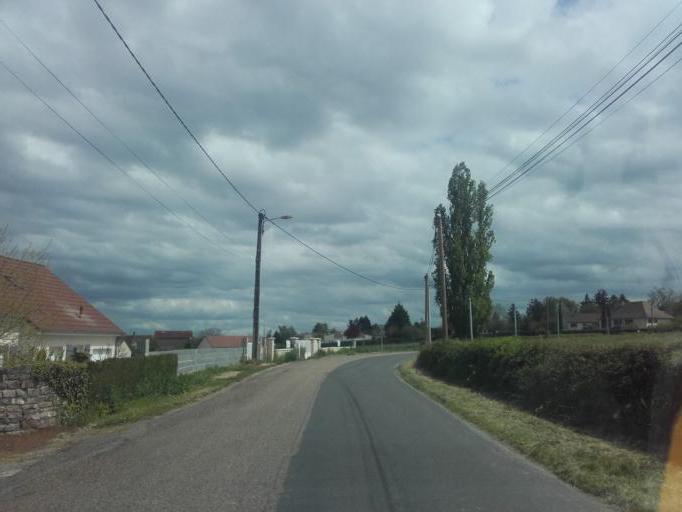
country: FR
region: Bourgogne
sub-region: Departement de Saone-et-Loire
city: Saint-Remy
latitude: 46.7545
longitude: 4.8183
